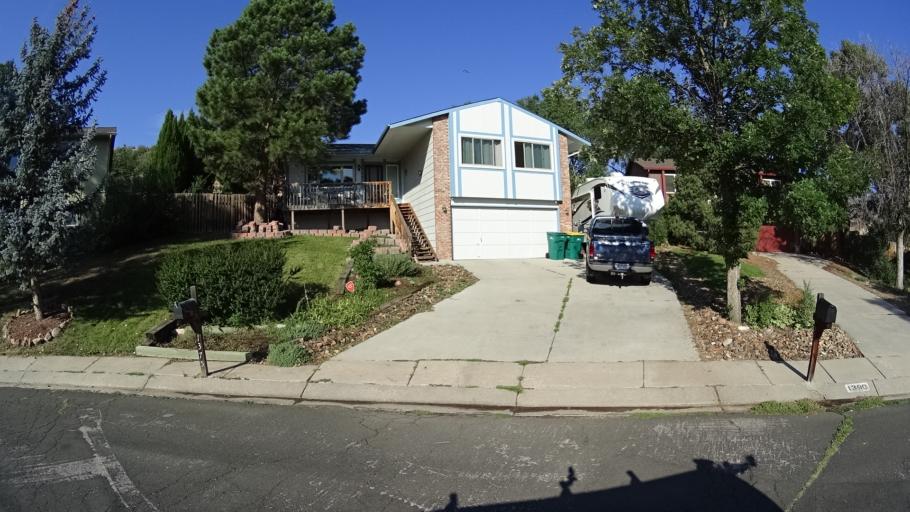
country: US
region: Colorado
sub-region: El Paso County
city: Colorado Springs
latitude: 38.8872
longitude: -104.8489
